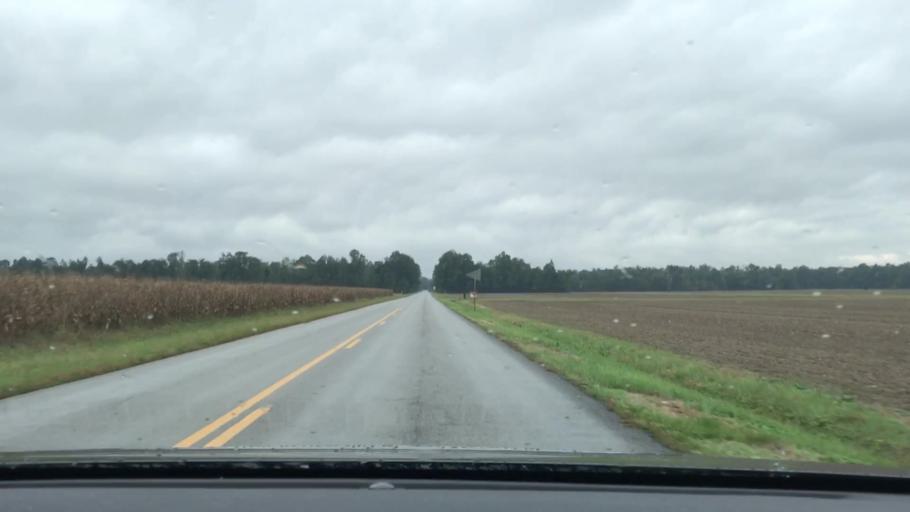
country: US
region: Kentucky
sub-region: McLean County
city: Calhoun
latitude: 37.3973
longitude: -87.2850
